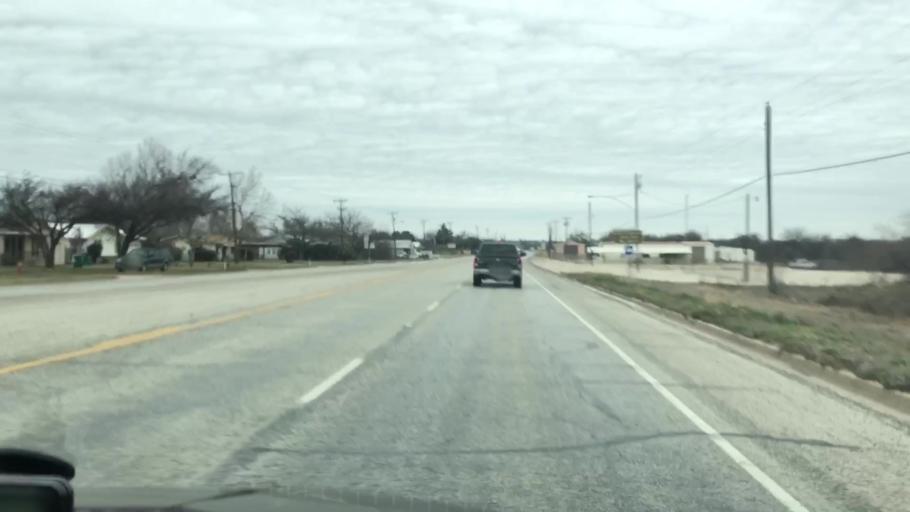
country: US
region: Texas
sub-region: Jack County
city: Jacksboro
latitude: 33.2050
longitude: -98.1530
